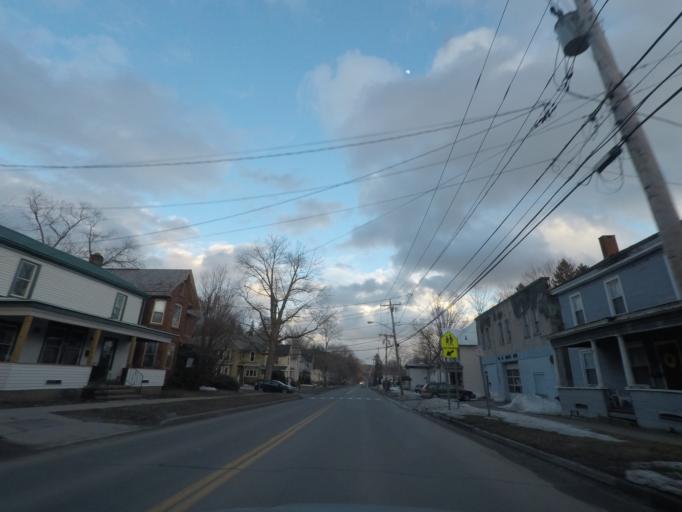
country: US
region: New York
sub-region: Montgomery County
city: Saint Johnsville
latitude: 42.9985
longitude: -74.6759
